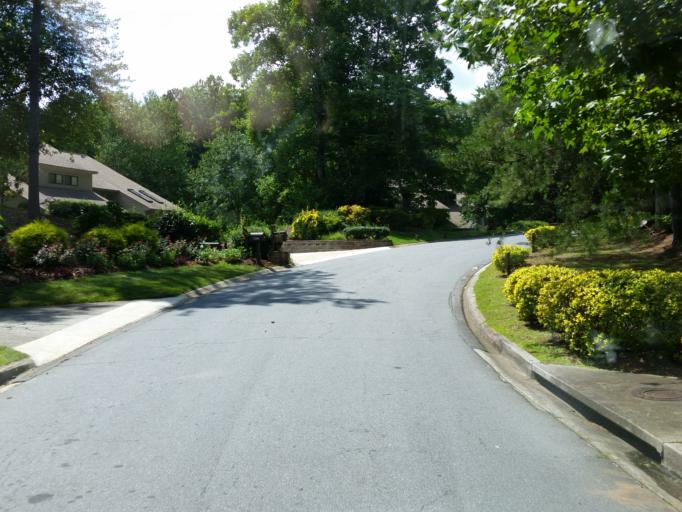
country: US
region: Georgia
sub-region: Fulton County
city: Roswell
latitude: 34.0468
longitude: -84.4298
